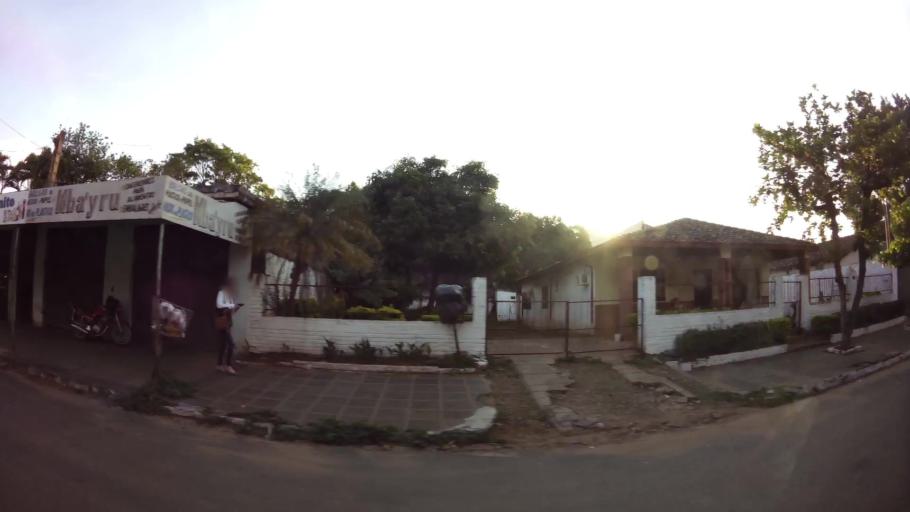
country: PY
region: Central
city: San Lorenzo
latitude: -25.3511
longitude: -57.5070
